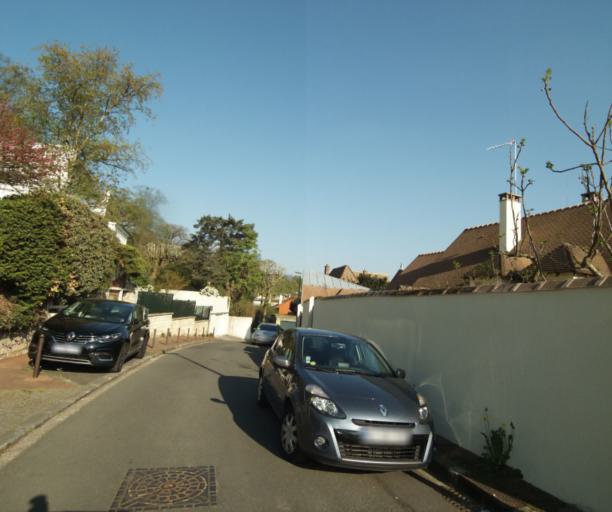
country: FR
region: Ile-de-France
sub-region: Departement des Hauts-de-Seine
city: Ville-d'Avray
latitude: 48.8288
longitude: 2.2052
